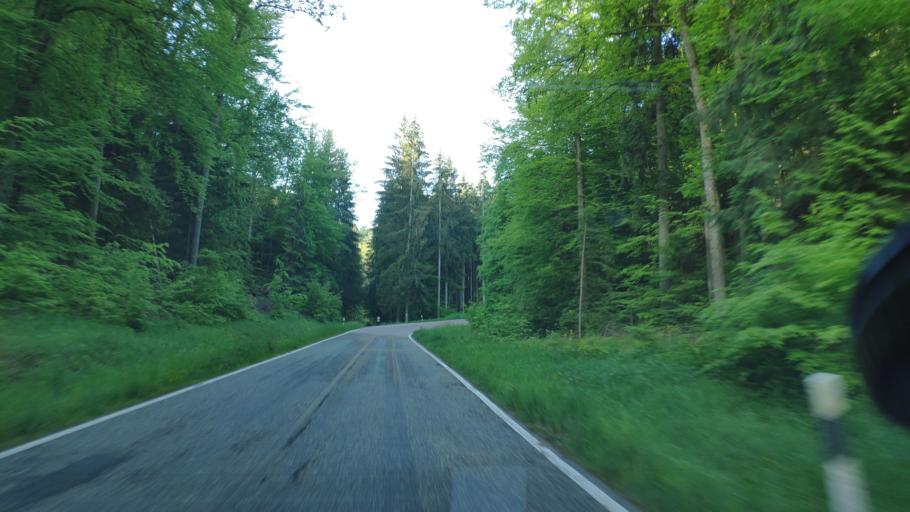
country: DE
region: Rheinland-Pfalz
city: Lemberg
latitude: 49.1526
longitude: 7.7096
